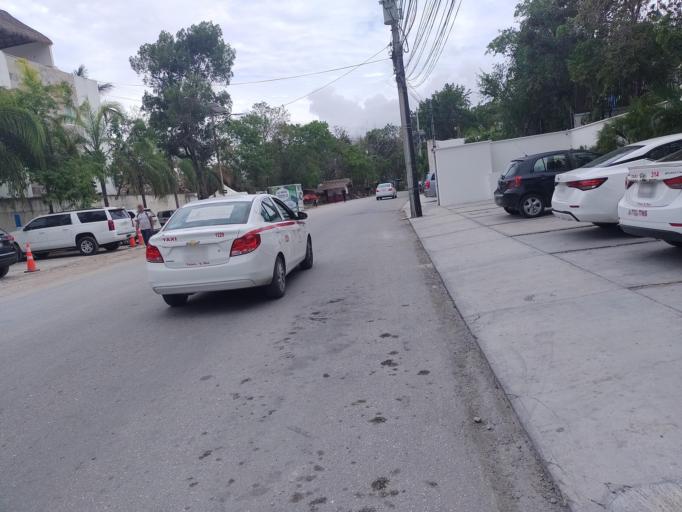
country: MX
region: Quintana Roo
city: Tulum
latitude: 20.2059
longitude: -87.4714
